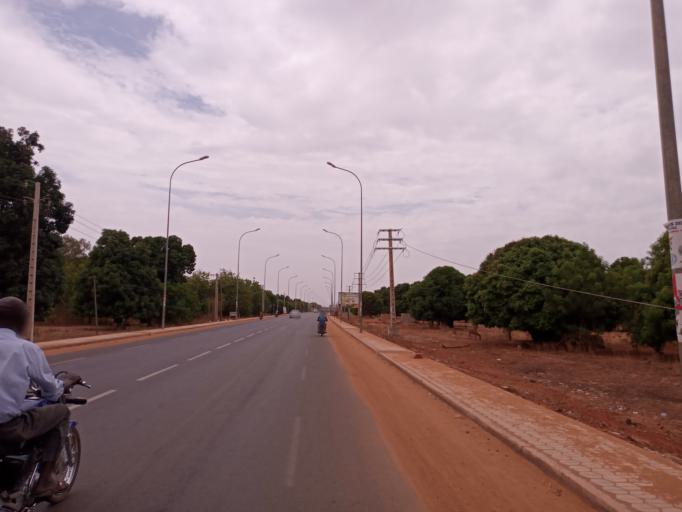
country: ML
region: Koulikoro
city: Koulikoro
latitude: 12.8500
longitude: -7.5733
